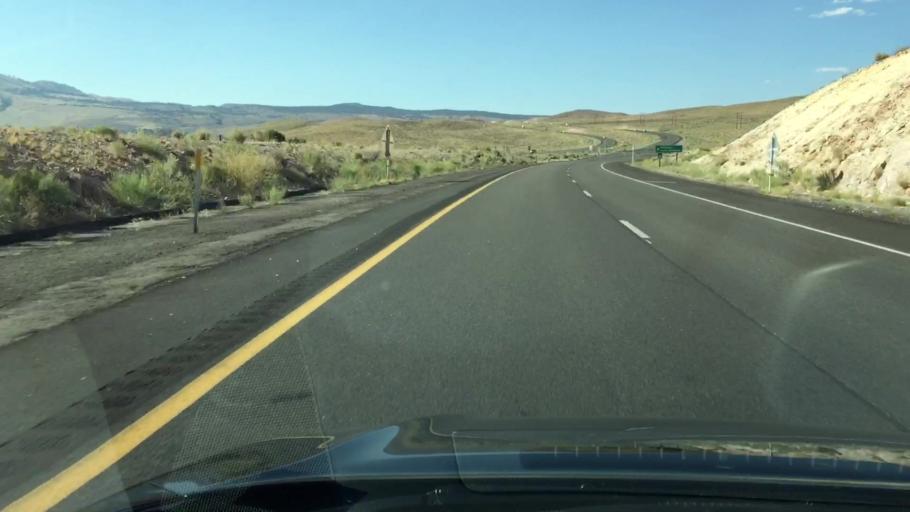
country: US
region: California
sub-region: Inyo County
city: West Bishop
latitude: 37.4429
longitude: -118.5713
